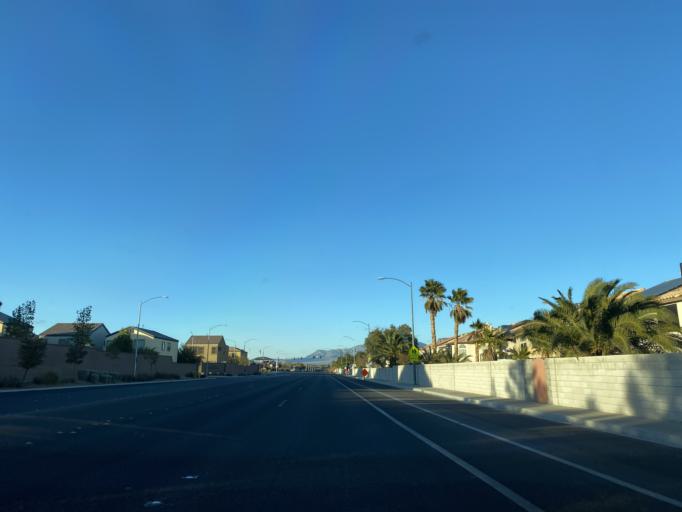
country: US
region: Nevada
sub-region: Clark County
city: Summerlin South
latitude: 36.2279
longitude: -115.2974
